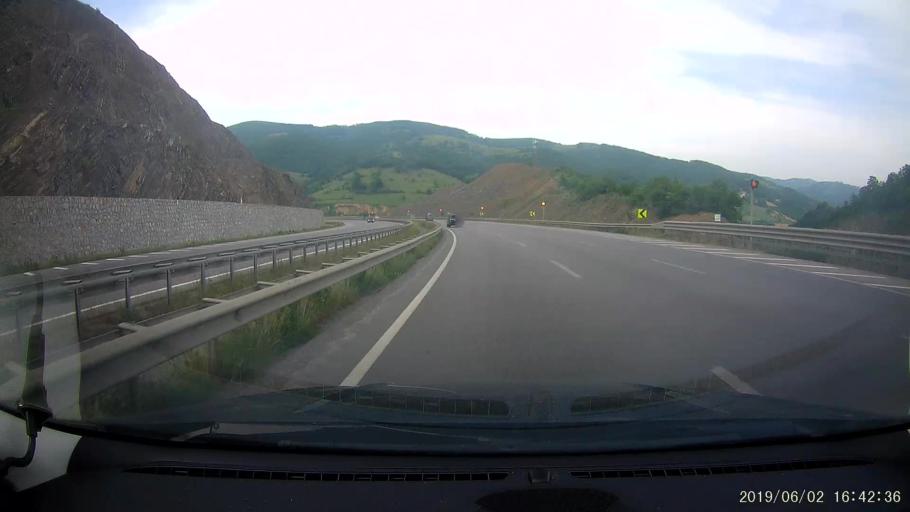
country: TR
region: Samsun
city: Kavak
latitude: 41.1205
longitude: 36.1361
